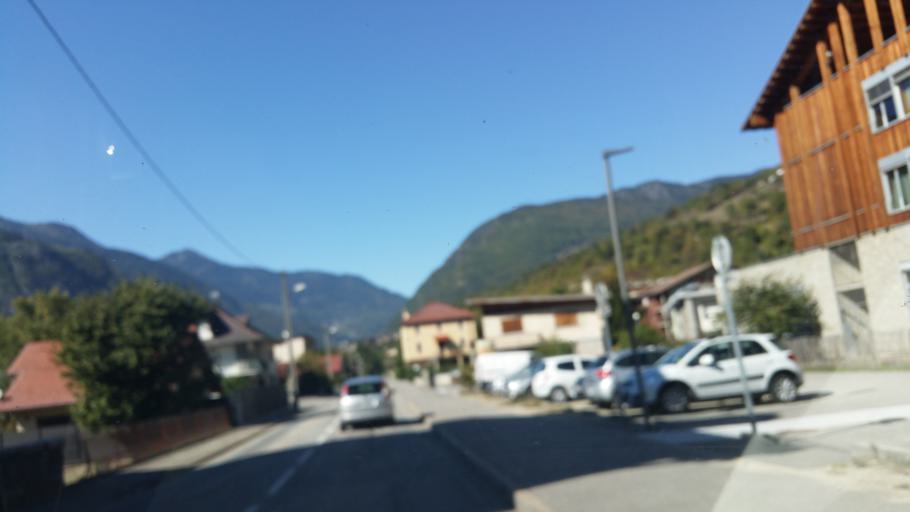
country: FR
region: Rhone-Alpes
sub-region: Departement de la Savoie
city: Aigueblanche
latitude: 45.5041
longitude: 6.5063
